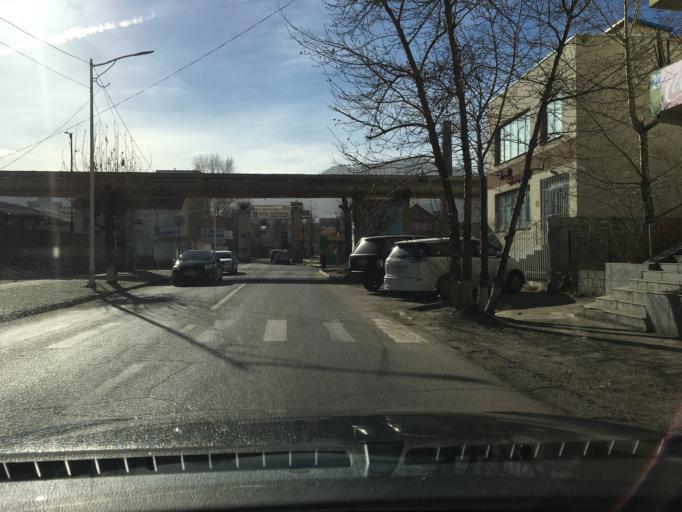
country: MN
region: Ulaanbaatar
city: Ulaanbaatar
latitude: 47.8963
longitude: 106.8961
